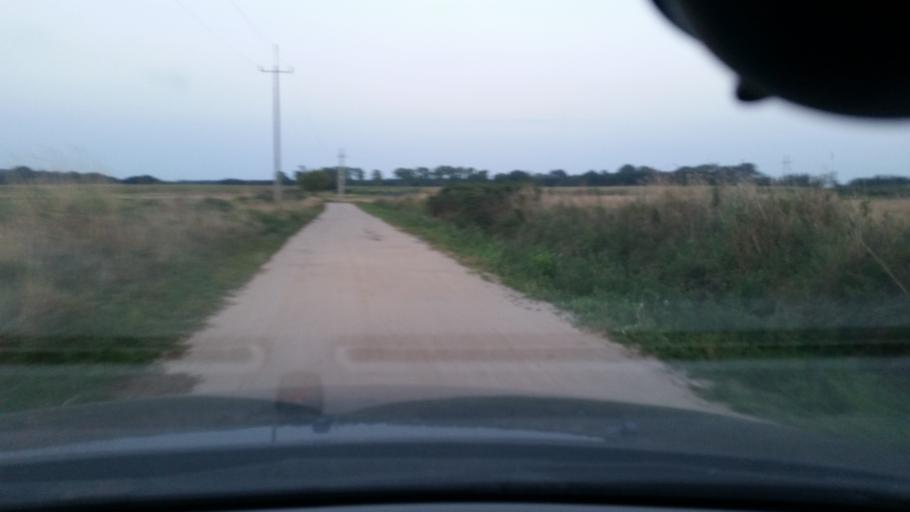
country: PL
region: Pomeranian Voivodeship
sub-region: Powiat wejherowski
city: Choczewo
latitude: 54.7760
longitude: 17.7922
